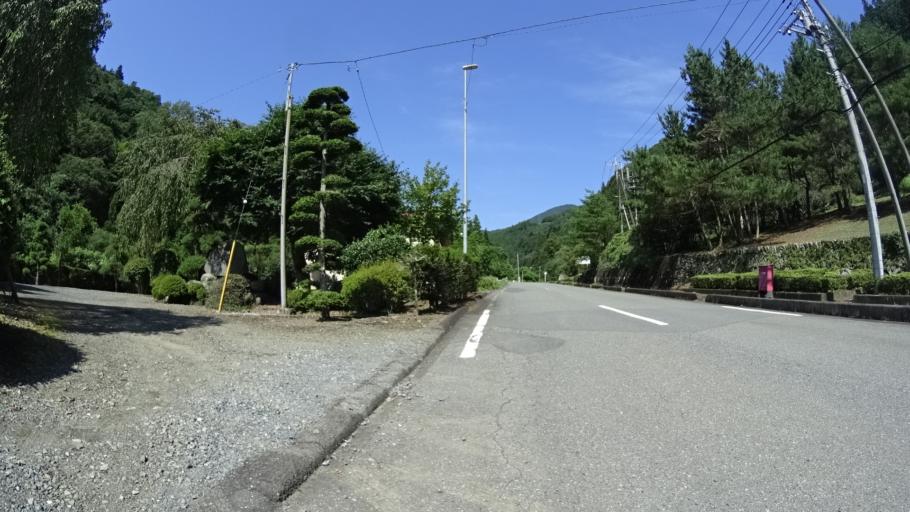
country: JP
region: Gunma
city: Tomioka
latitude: 36.0521
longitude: 138.8719
